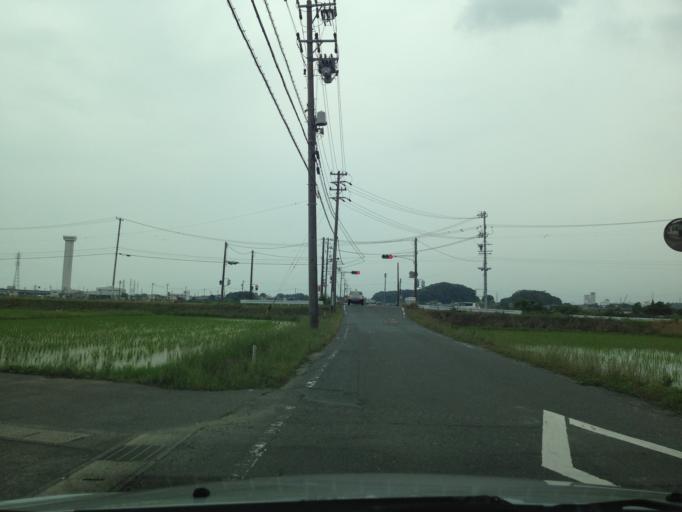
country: JP
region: Shizuoka
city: Fukuroi
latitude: 34.7622
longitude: 137.9369
